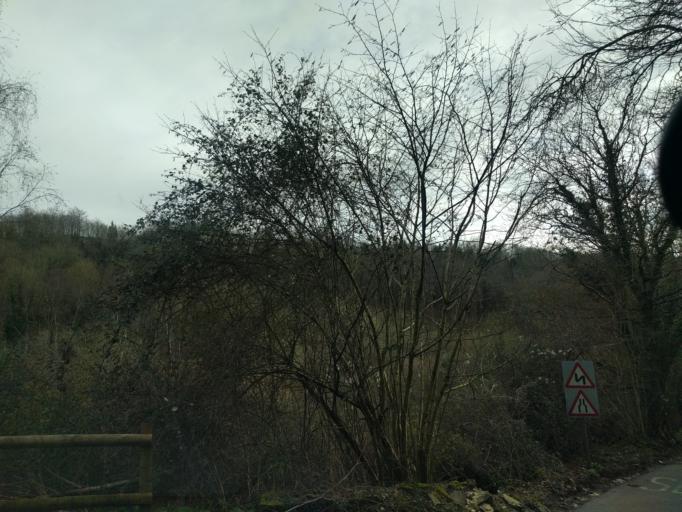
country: GB
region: England
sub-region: Wiltshire
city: Colerne
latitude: 51.4596
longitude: -2.2837
